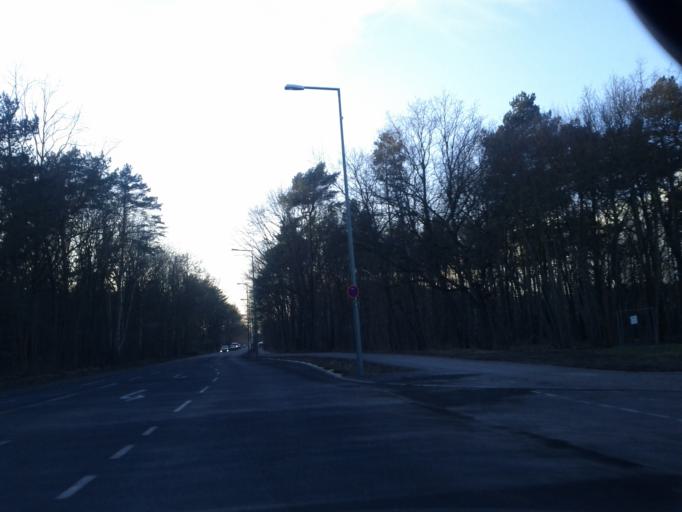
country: DE
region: Berlin
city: Adlershof
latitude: 52.4489
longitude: 13.5488
